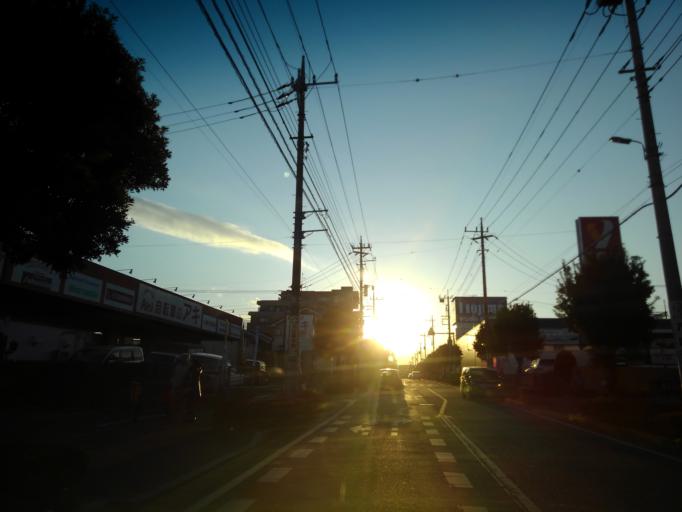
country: JP
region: Saitama
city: Tokorozawa
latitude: 35.7962
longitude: 139.5104
